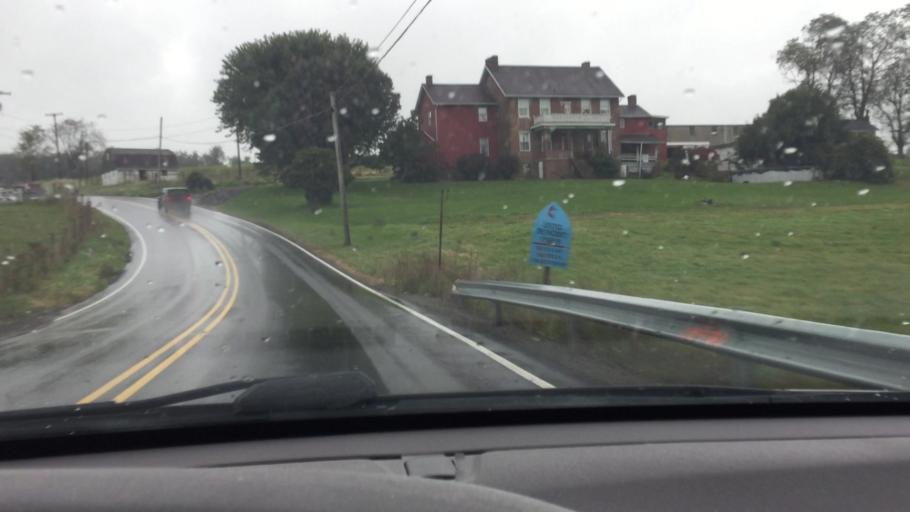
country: US
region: Pennsylvania
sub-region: Westmoreland County
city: Fellsburg
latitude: 40.1687
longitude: -79.8180
